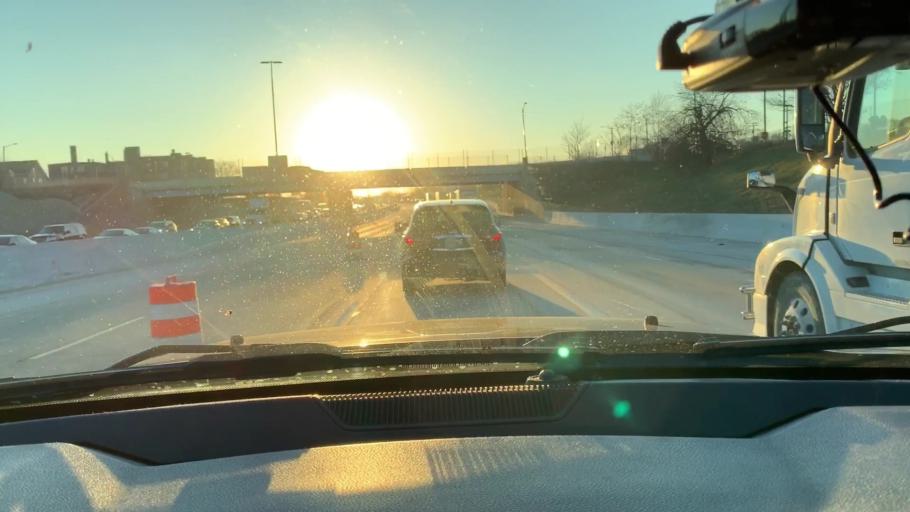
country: US
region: Michigan
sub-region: Wayne County
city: Detroit
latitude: 42.3117
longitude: -83.0961
